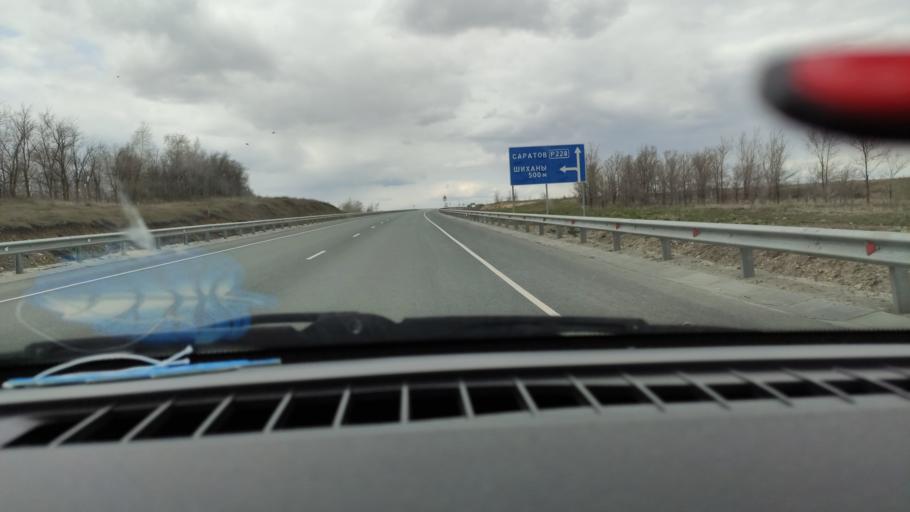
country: RU
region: Saratov
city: Shikhany
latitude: 52.1295
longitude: 47.2330
